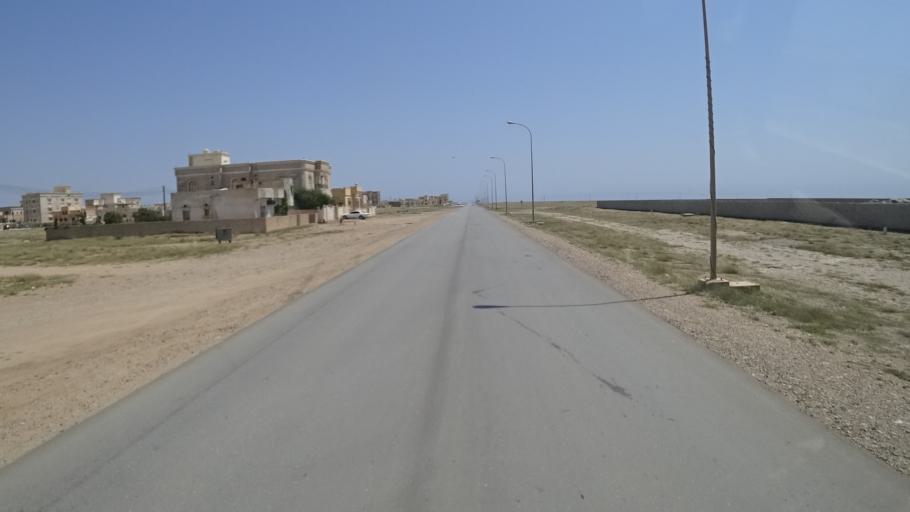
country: OM
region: Zufar
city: Salalah
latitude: 16.9832
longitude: 54.7032
